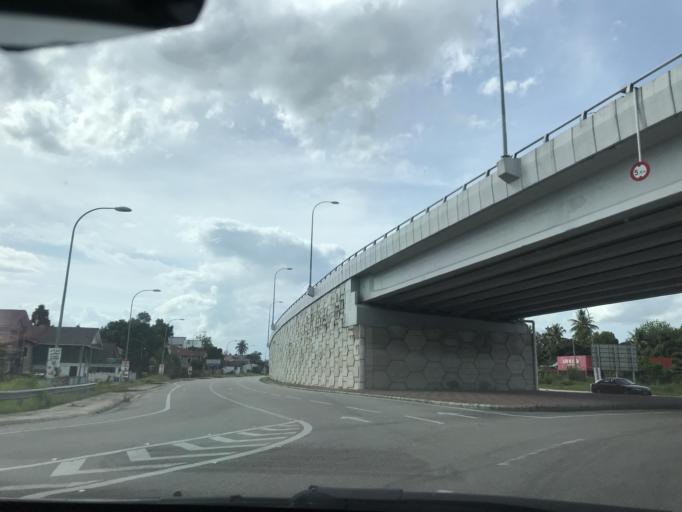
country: MY
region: Kelantan
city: Kampung Lemal
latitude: 6.0299
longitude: 102.1419
